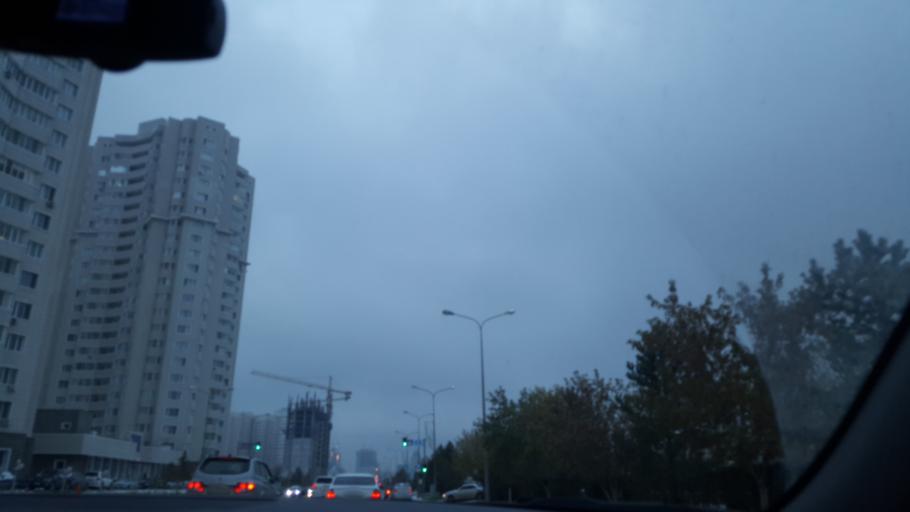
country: KZ
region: Astana Qalasy
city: Astana
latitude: 51.1202
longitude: 71.4658
